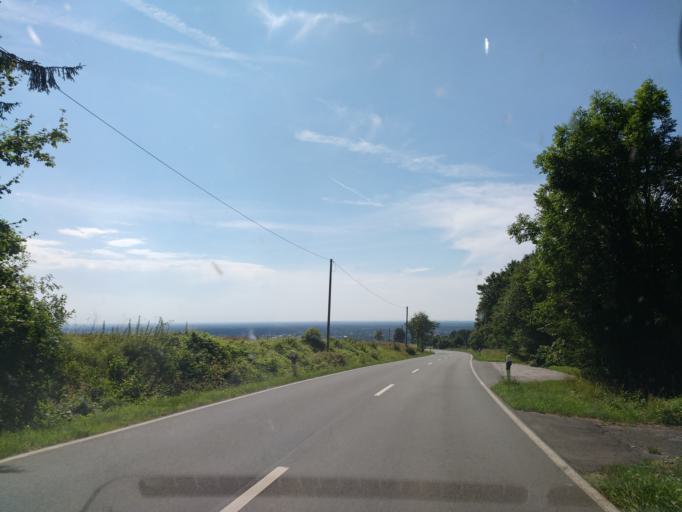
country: DE
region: North Rhine-Westphalia
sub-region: Regierungsbezirk Detmold
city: Schlangen
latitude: 51.8075
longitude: 8.8753
